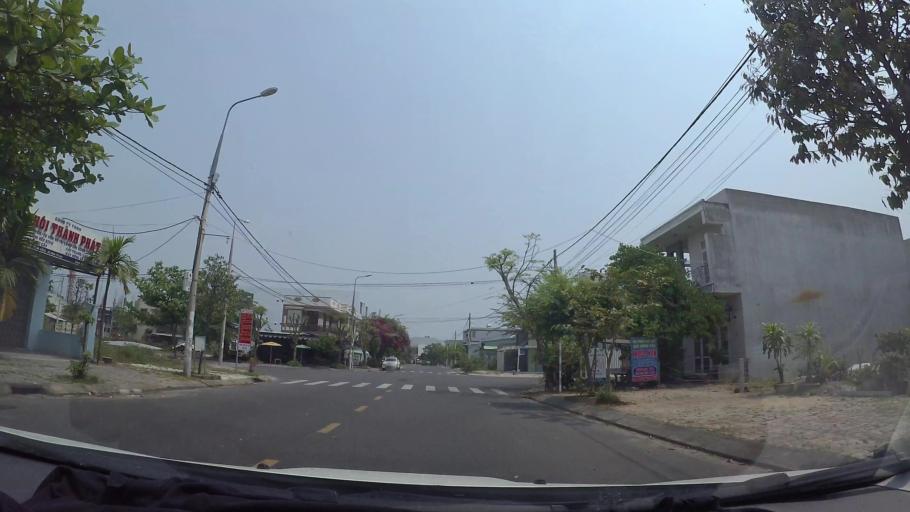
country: VN
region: Da Nang
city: Cam Le
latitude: 16.0014
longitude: 108.2210
